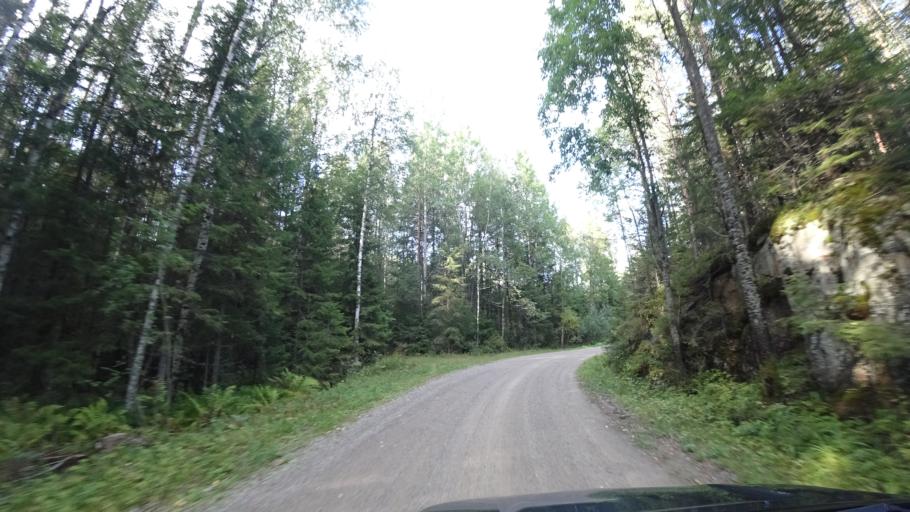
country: FI
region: Paijanne Tavastia
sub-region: Lahti
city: Auttoinen
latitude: 61.2197
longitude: 25.1793
